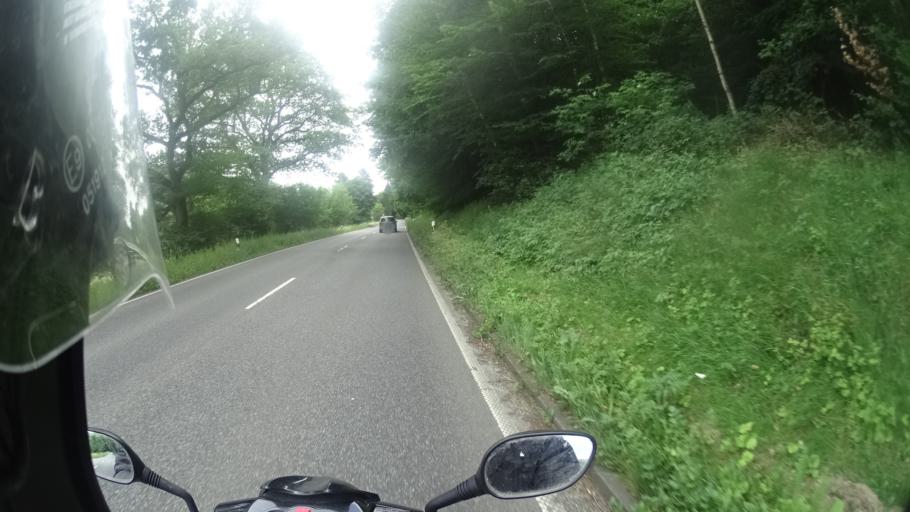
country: DE
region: Hesse
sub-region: Regierungsbezirk Darmstadt
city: Walluf
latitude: 50.0974
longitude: 8.1811
